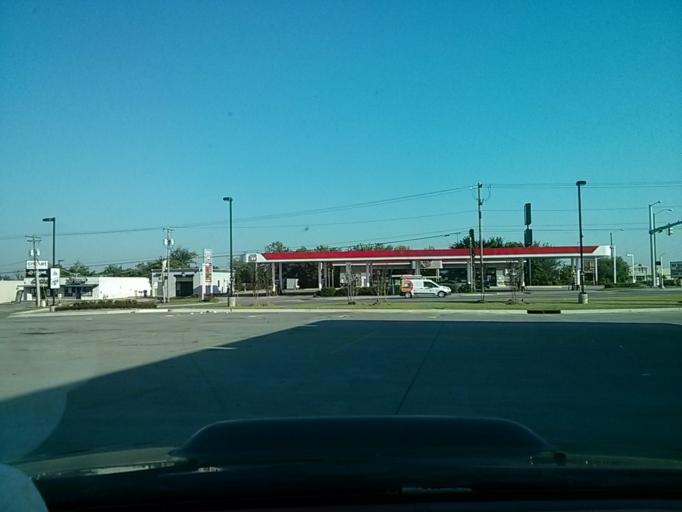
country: US
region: Oklahoma
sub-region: Tulsa County
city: Tulsa
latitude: 36.1602
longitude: -95.8872
